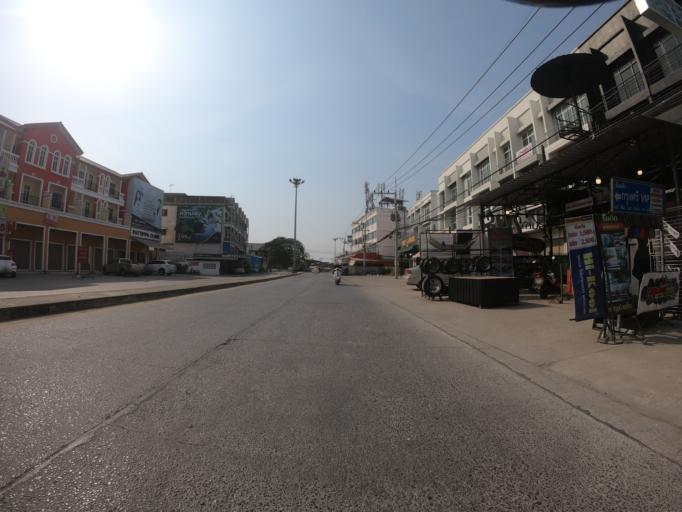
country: TH
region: Phra Nakhon Si Ayutthaya
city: Phra Nakhon Si Ayutthaya
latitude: 14.3392
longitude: 100.6005
